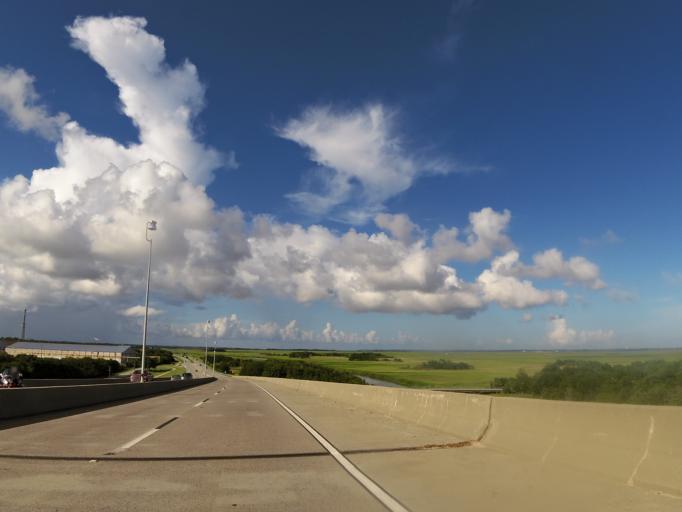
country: US
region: Georgia
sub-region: Glynn County
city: Brunswick
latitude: 31.1239
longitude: -81.4810
